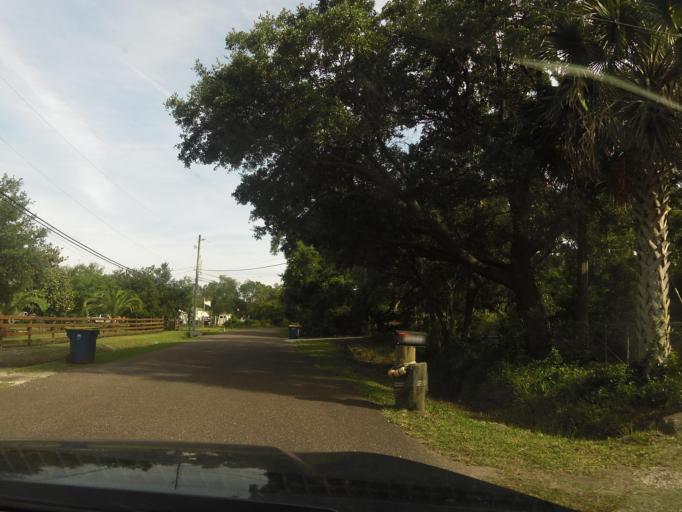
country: US
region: Florida
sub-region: Nassau County
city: Fernandina Beach
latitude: 30.5232
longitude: -81.4936
